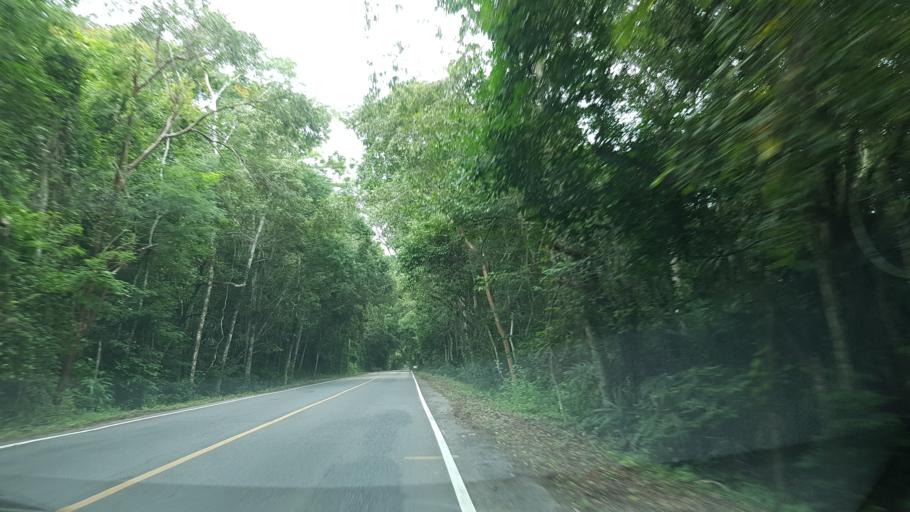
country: GT
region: Peten
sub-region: Municipio de San Jose
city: San Jose
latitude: 17.1756
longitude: -89.6406
